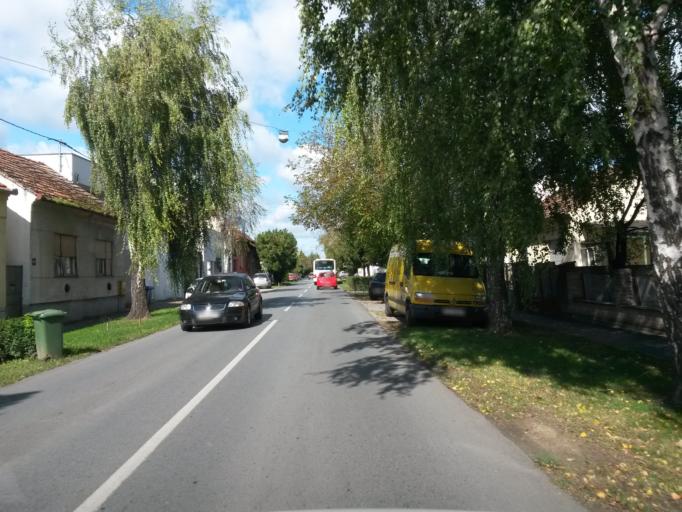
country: HR
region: Osjecko-Baranjska
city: Visnjevac
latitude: 45.5593
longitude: 18.6478
